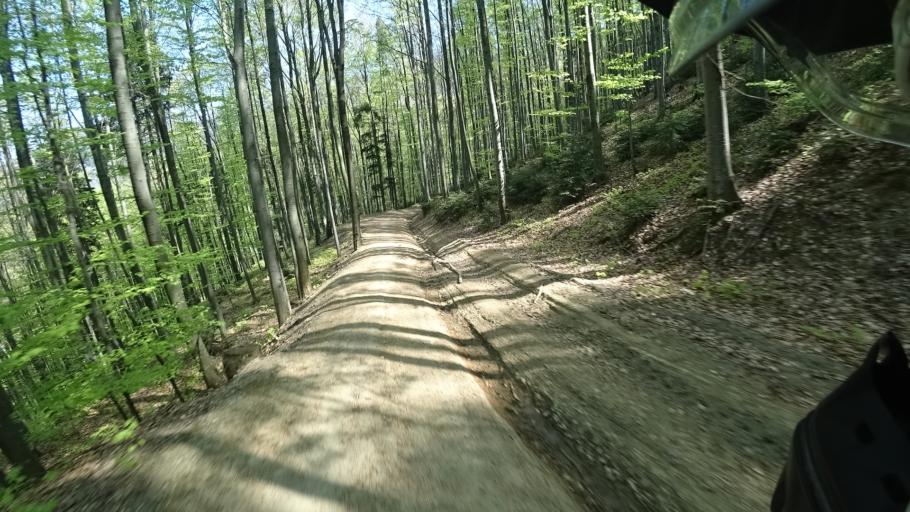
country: HR
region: Zagrebacka
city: Jablanovec
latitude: 45.9003
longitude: 15.9187
